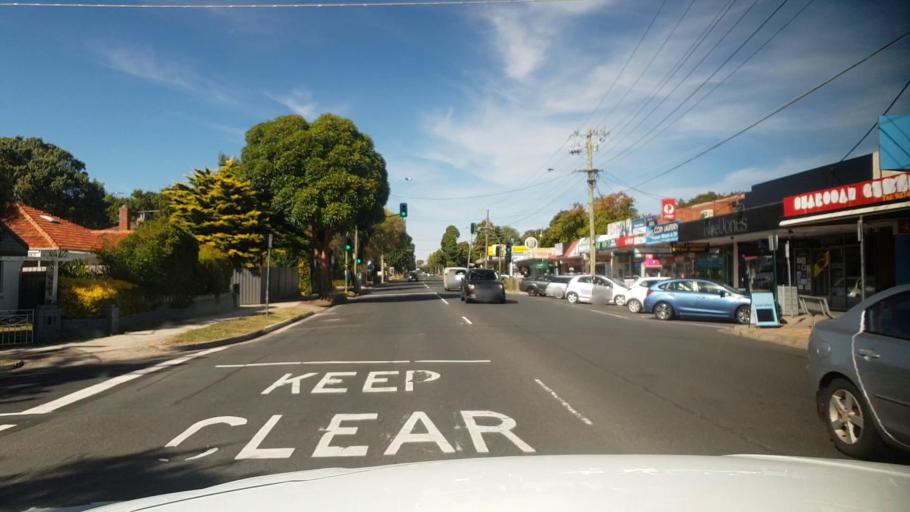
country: AU
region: Victoria
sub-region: Whitehorse
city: Vermont
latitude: -37.8270
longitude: 145.1946
